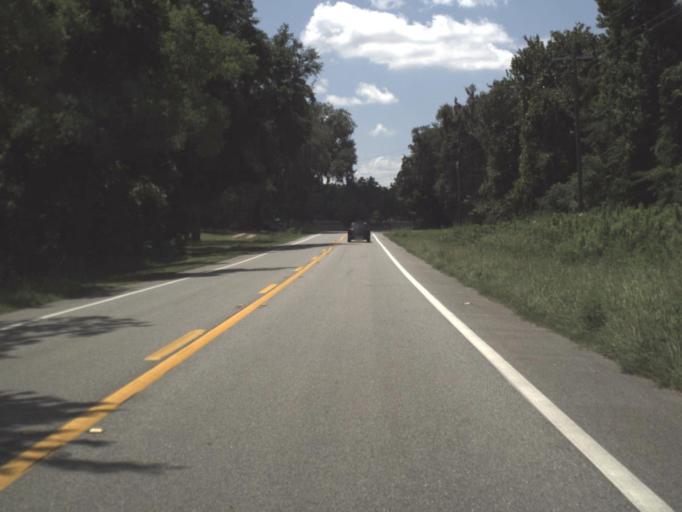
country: US
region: Florida
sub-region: Madison County
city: Madison
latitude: 30.5323
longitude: -83.6320
